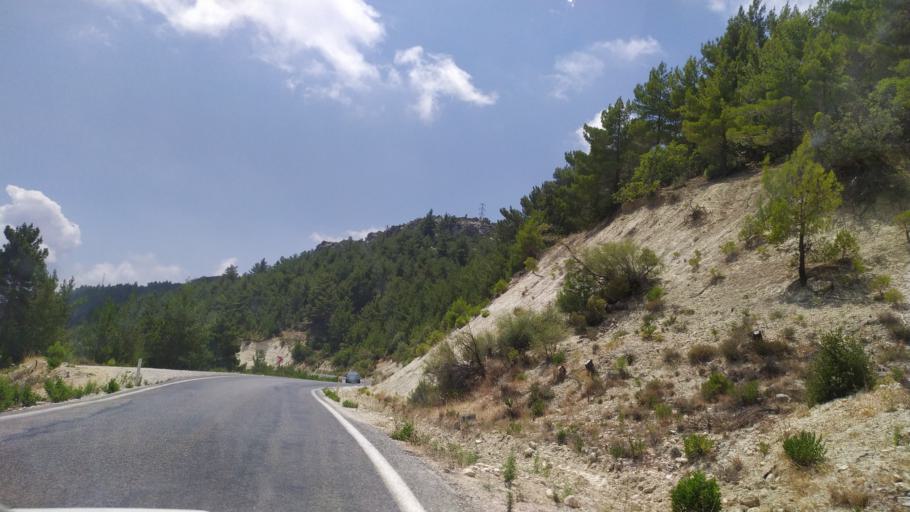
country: TR
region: Mersin
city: Gulnar
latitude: 36.2990
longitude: 33.3801
